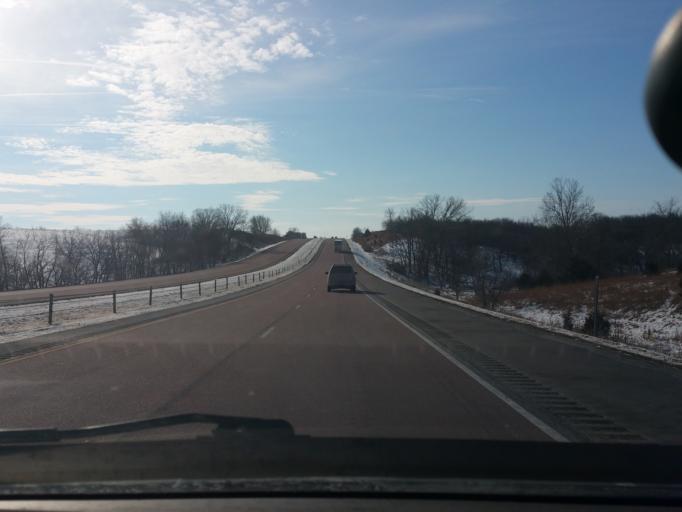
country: US
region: Iowa
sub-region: Madison County
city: Buffalo (historical)
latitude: 41.2696
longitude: -93.7797
